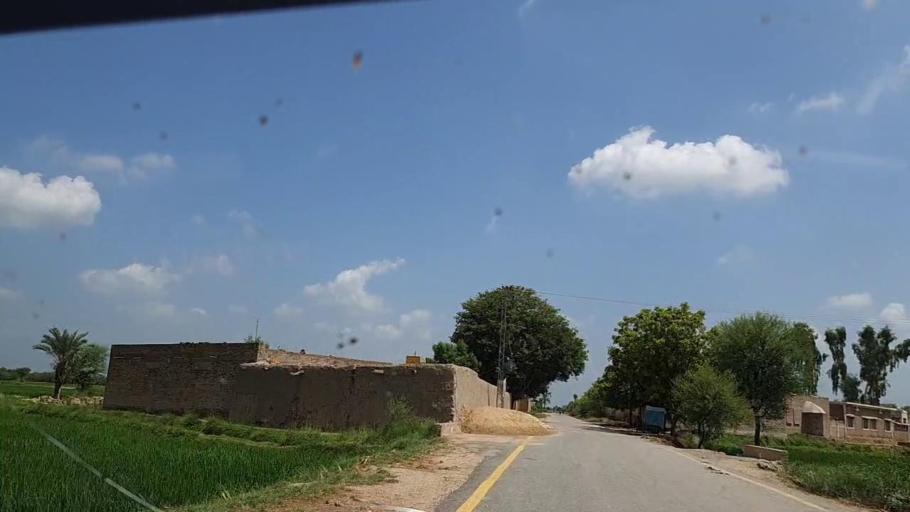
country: PK
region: Sindh
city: Tharu Shah
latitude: 26.9786
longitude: 68.0846
